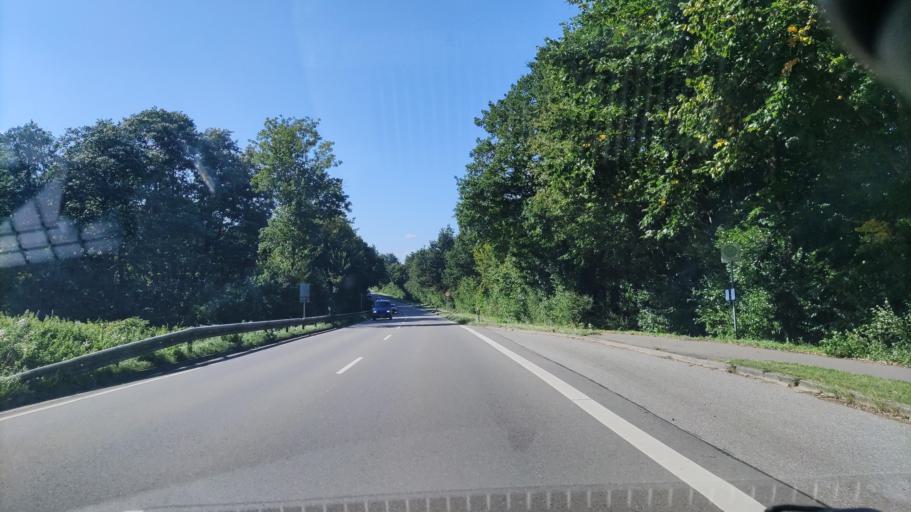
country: DE
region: Schleswig-Holstein
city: Windeby
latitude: 54.4629
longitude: 9.8160
